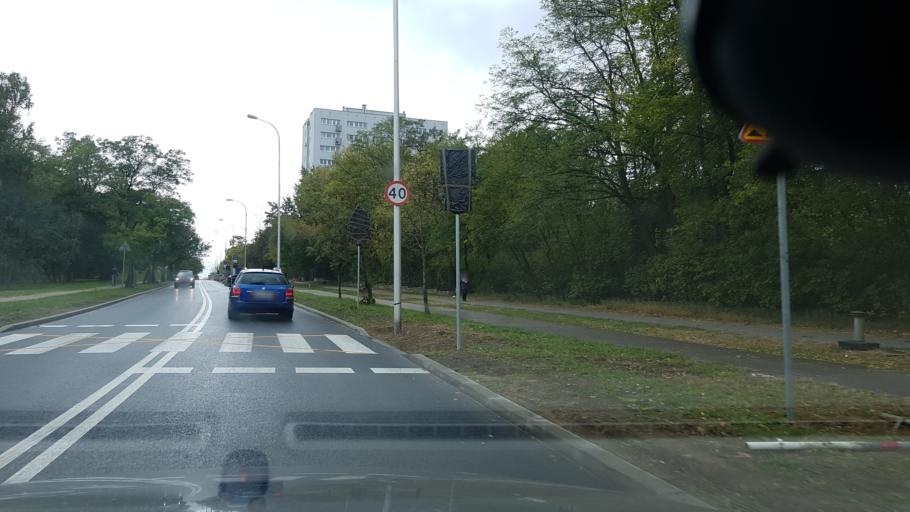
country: PL
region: Masovian Voivodeship
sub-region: Warszawa
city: Zoliborz
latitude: 52.2835
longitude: 20.9656
